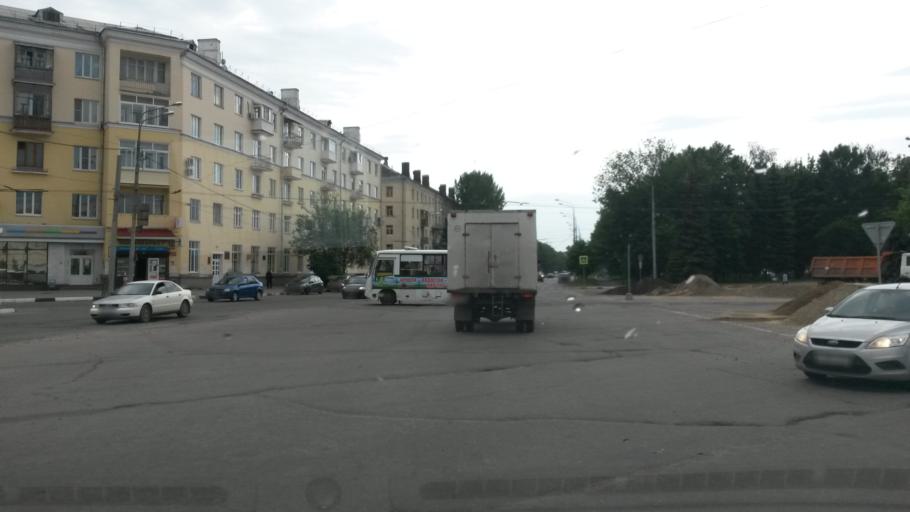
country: RU
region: Jaroslavl
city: Yaroslavl
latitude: 57.6337
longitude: 39.8597
